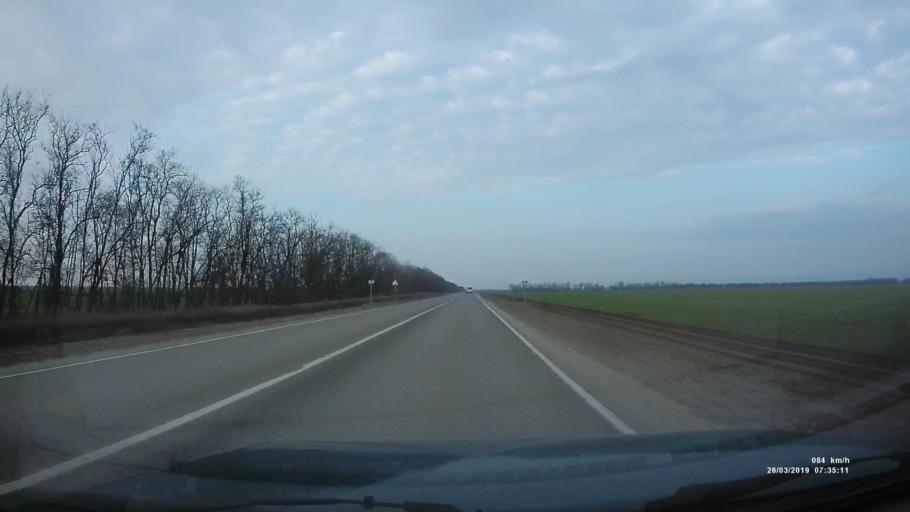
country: RU
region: Rostov
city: Novobessergenovka
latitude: 47.2084
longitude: 38.7436
